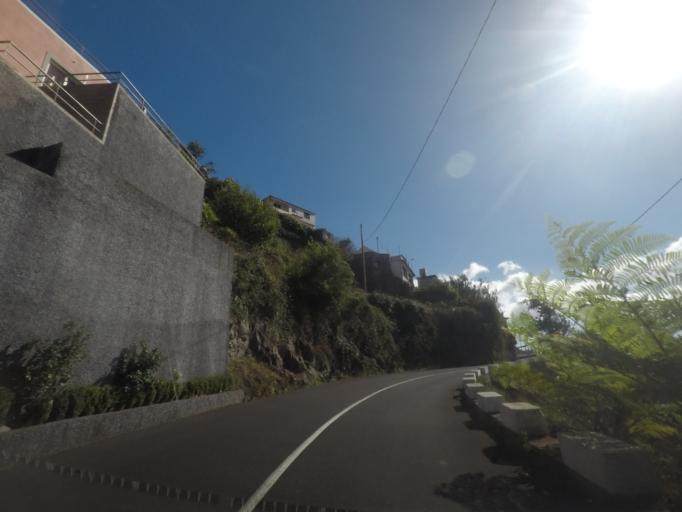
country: PT
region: Madeira
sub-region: Ribeira Brava
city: Campanario
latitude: 32.6672
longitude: -17.0224
